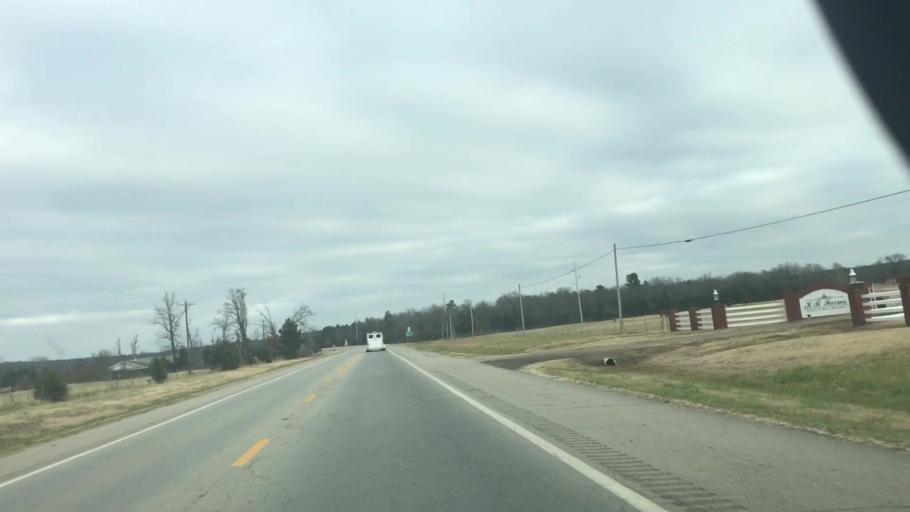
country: US
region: Arkansas
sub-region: Scott County
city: Waldron
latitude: 34.9362
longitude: -94.1022
